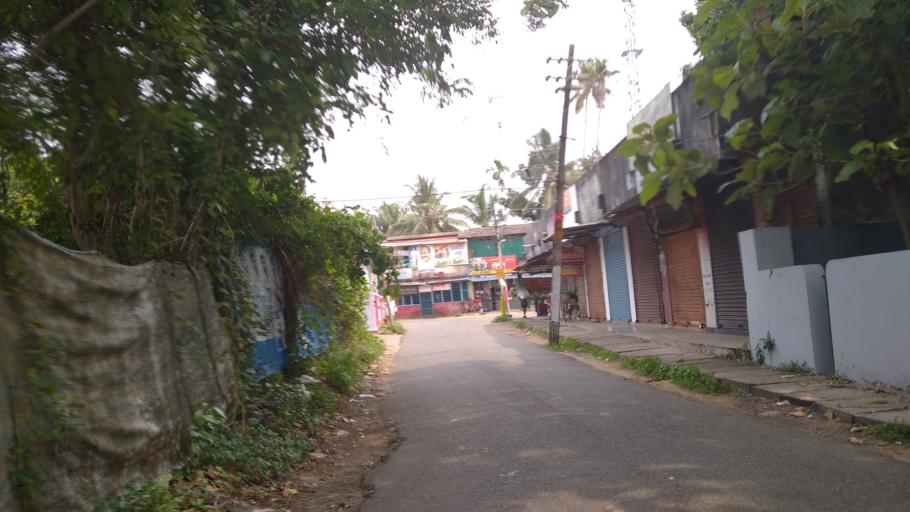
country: IN
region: Kerala
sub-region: Ernakulam
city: Elur
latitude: 10.1467
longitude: 76.2545
